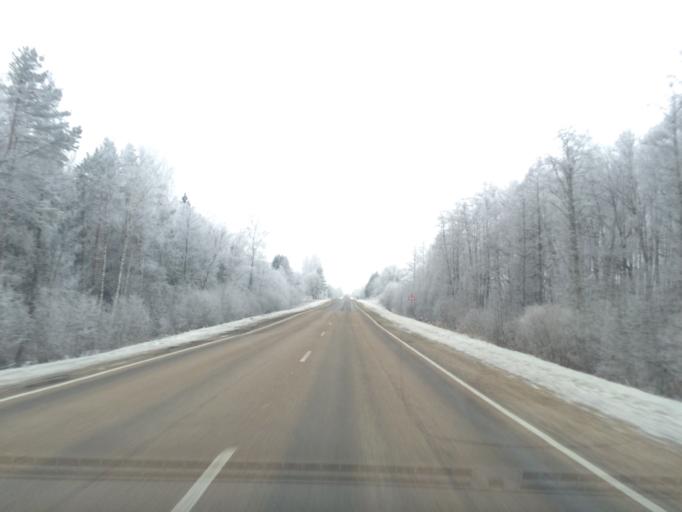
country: LV
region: Rezekne
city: Rezekne
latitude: 56.6445
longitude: 27.4870
